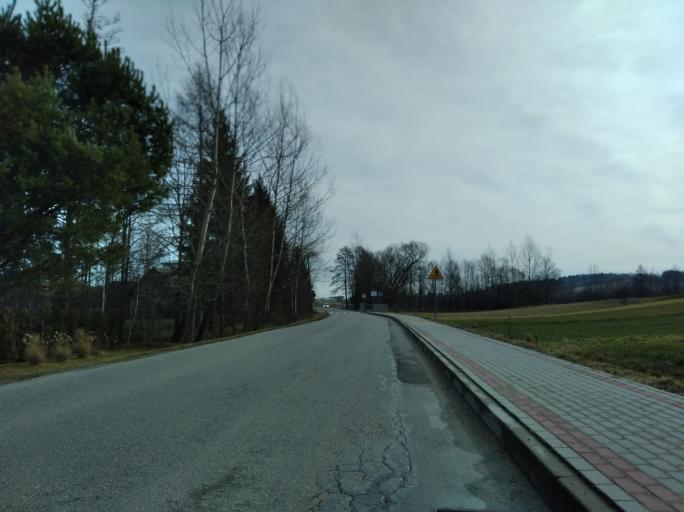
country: PL
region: Subcarpathian Voivodeship
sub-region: Powiat brzozowski
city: Orzechowka
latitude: 49.7271
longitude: 21.9485
